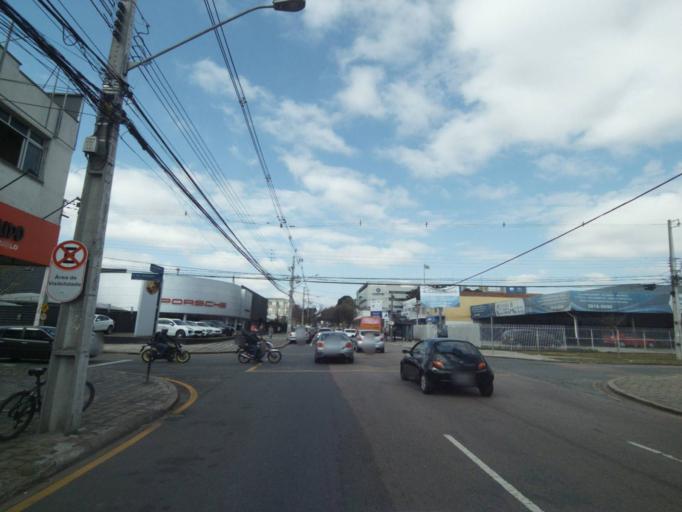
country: BR
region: Parana
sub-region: Curitiba
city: Curitiba
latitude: -25.4473
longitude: -49.2661
